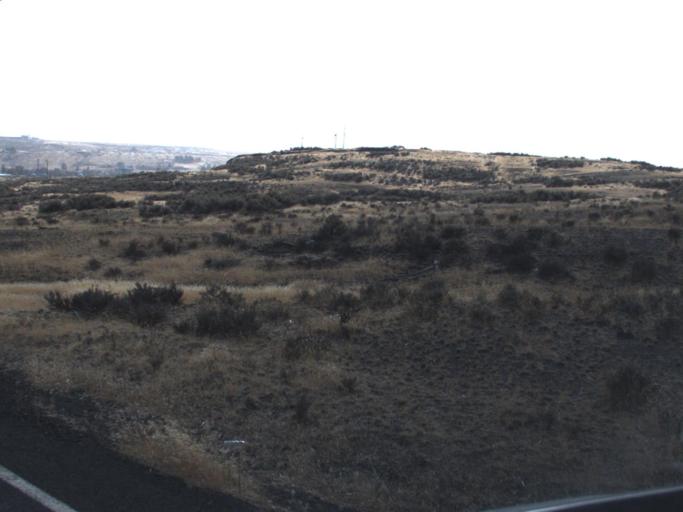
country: US
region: Washington
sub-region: Adams County
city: Ritzville
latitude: 47.3500
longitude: -118.6951
